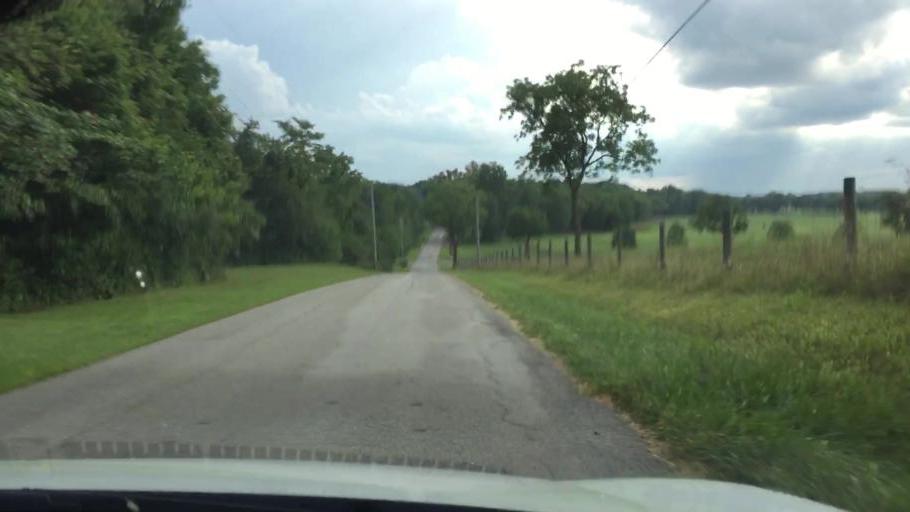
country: US
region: Ohio
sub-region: Champaign County
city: Mechanicsburg
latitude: 40.0112
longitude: -83.6472
